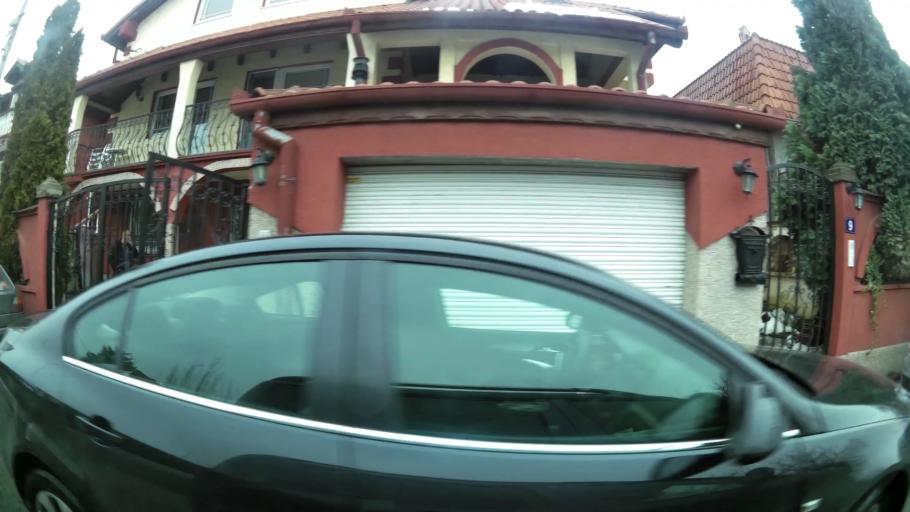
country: RS
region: Central Serbia
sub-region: Belgrade
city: Vozdovac
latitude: 44.7615
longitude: 20.4972
